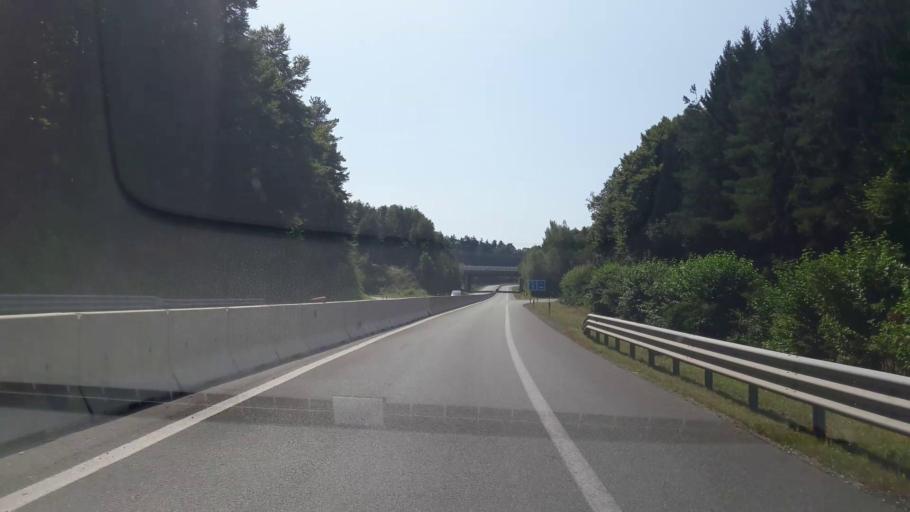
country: AT
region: Styria
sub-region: Politischer Bezirk Hartberg-Fuerstenfeld
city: Sankt Johann in der Haide
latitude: 47.2768
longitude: 16.0105
